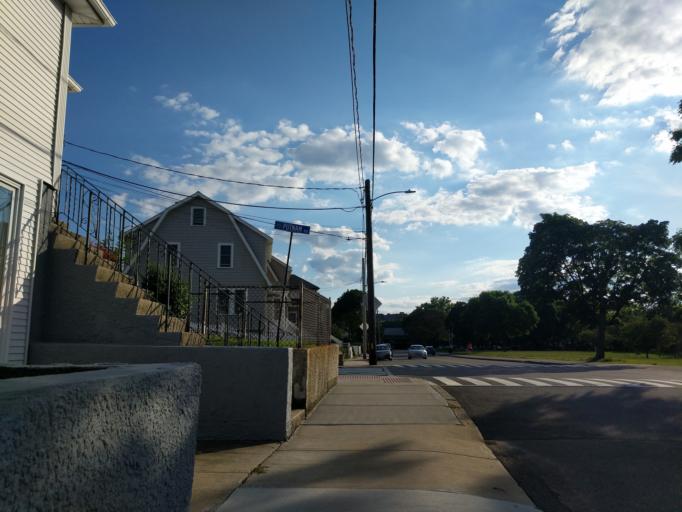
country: US
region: Massachusetts
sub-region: Middlesex County
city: Somerville
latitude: 42.3987
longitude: -71.0882
